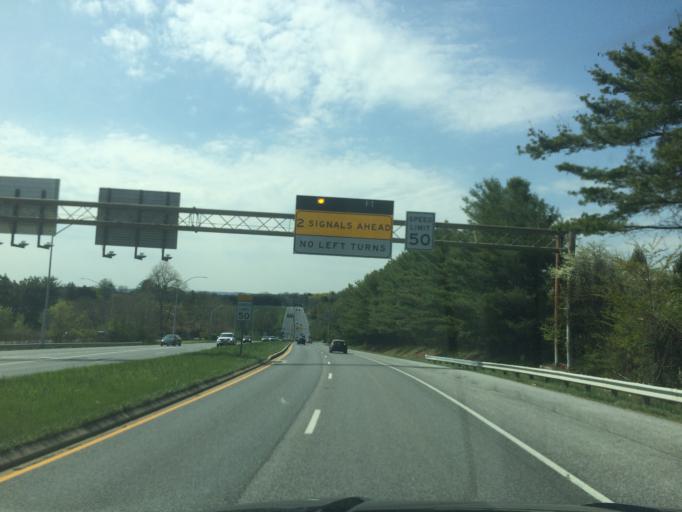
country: US
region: Maryland
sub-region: Baltimore County
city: Reisterstown
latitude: 39.4767
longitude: -76.8434
